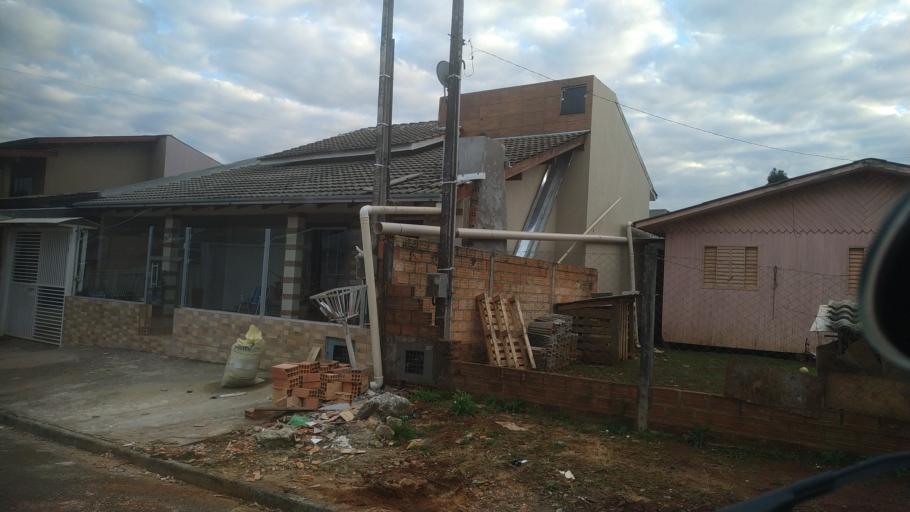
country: BR
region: Santa Catarina
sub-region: Chapeco
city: Chapeco
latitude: -27.1031
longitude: -52.6790
